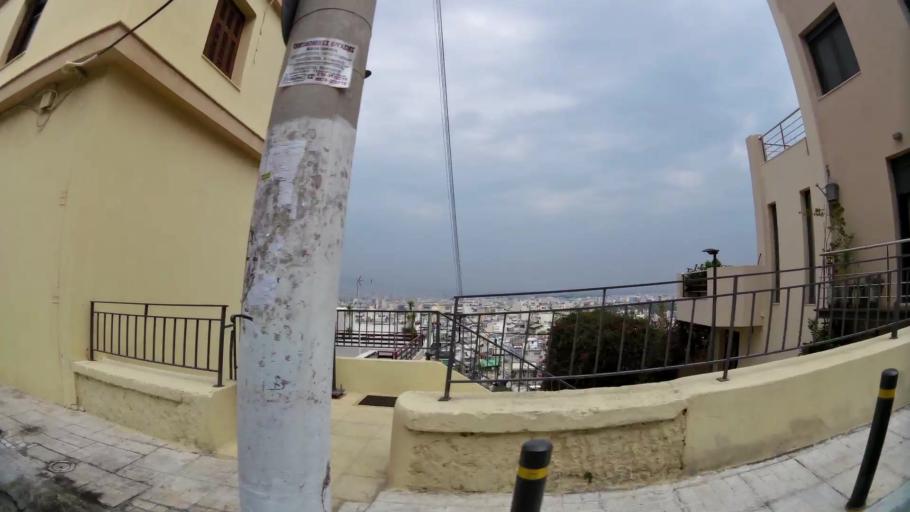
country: GR
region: Attica
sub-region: Nomos Attikis
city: Piraeus
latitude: 37.9422
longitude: 23.6565
